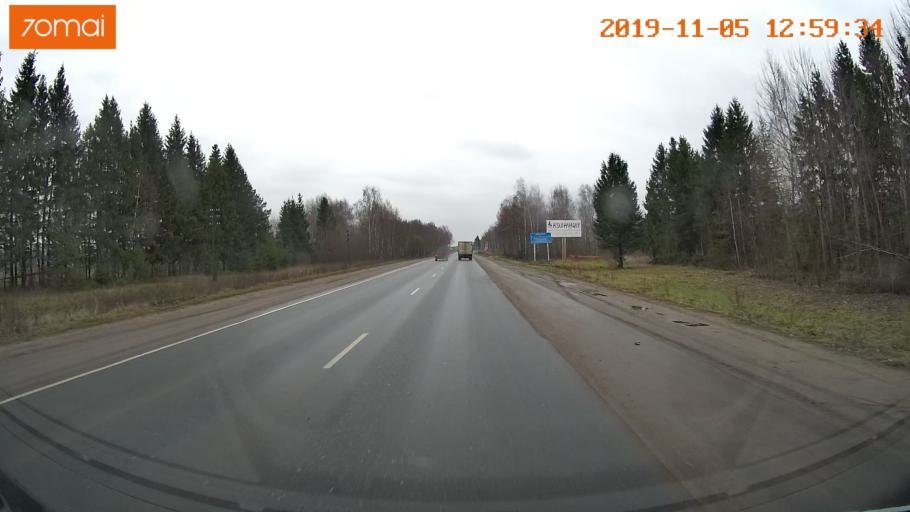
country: RU
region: Ivanovo
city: Kokhma
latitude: 56.9178
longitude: 41.1314
